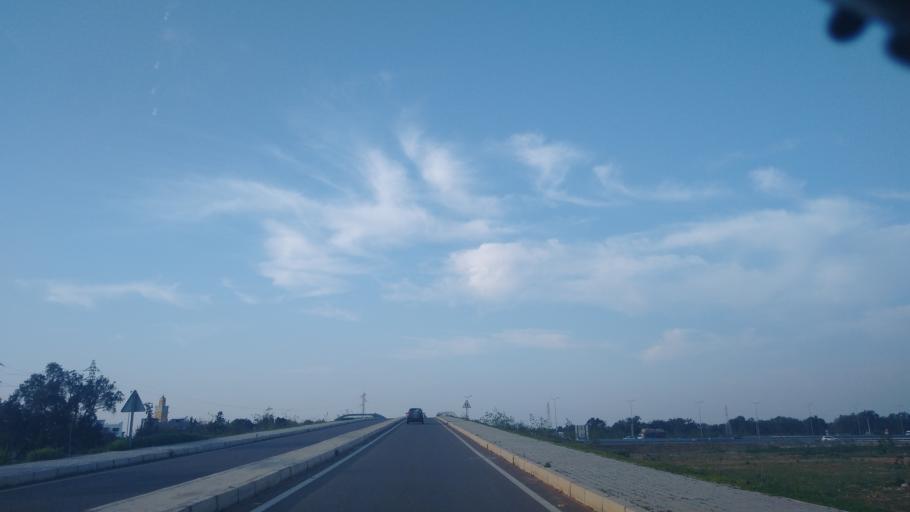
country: MA
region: Rabat-Sale-Zemmour-Zaer
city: Sale
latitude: 33.9988
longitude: -6.7185
